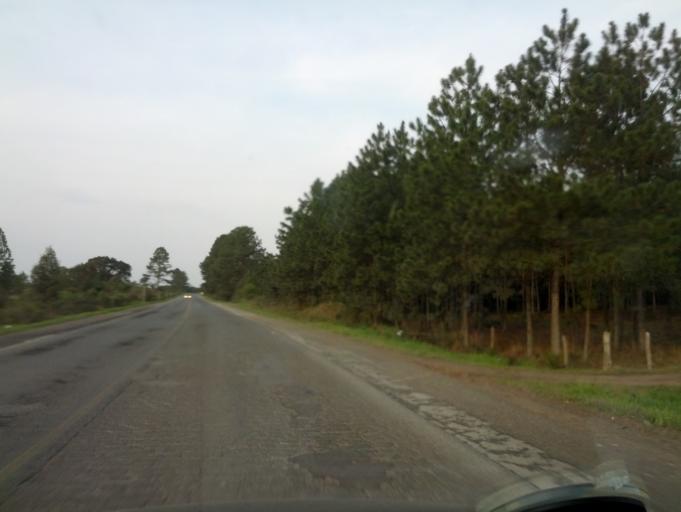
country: BR
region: Santa Catarina
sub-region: Otacilio Costa
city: Otacilio Costa
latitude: -27.3095
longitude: -50.1181
